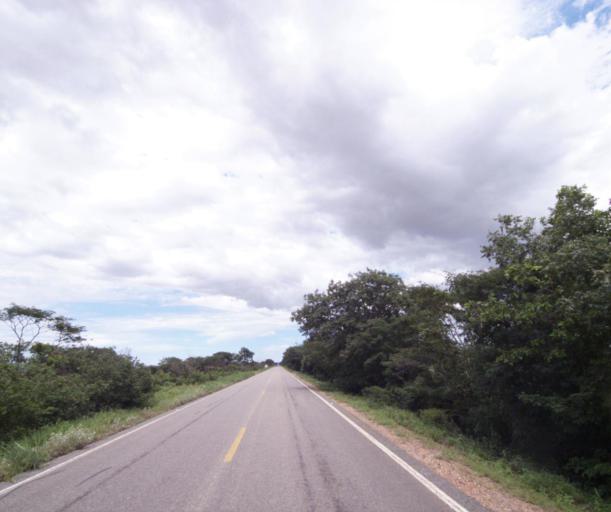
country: BR
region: Bahia
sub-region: Palmas De Monte Alto
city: Palmas de Monte Alto
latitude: -14.2644
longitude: -43.3443
